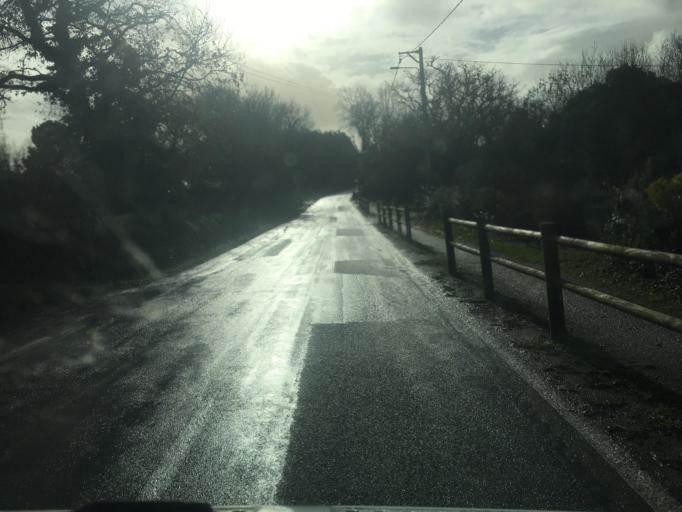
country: FR
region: Brittany
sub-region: Departement du Morbihan
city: Sarzeau
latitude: 47.5079
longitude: -2.7719
